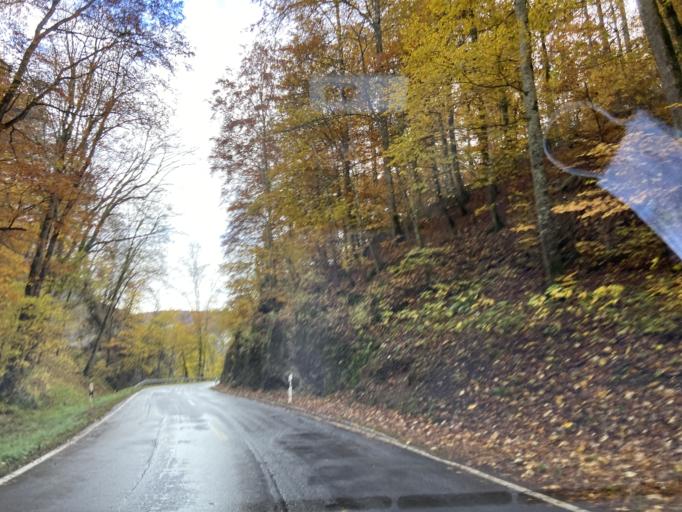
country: DE
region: Baden-Wuerttemberg
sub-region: Tuebingen Region
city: Schwenningen
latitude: 48.0905
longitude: 9.0298
